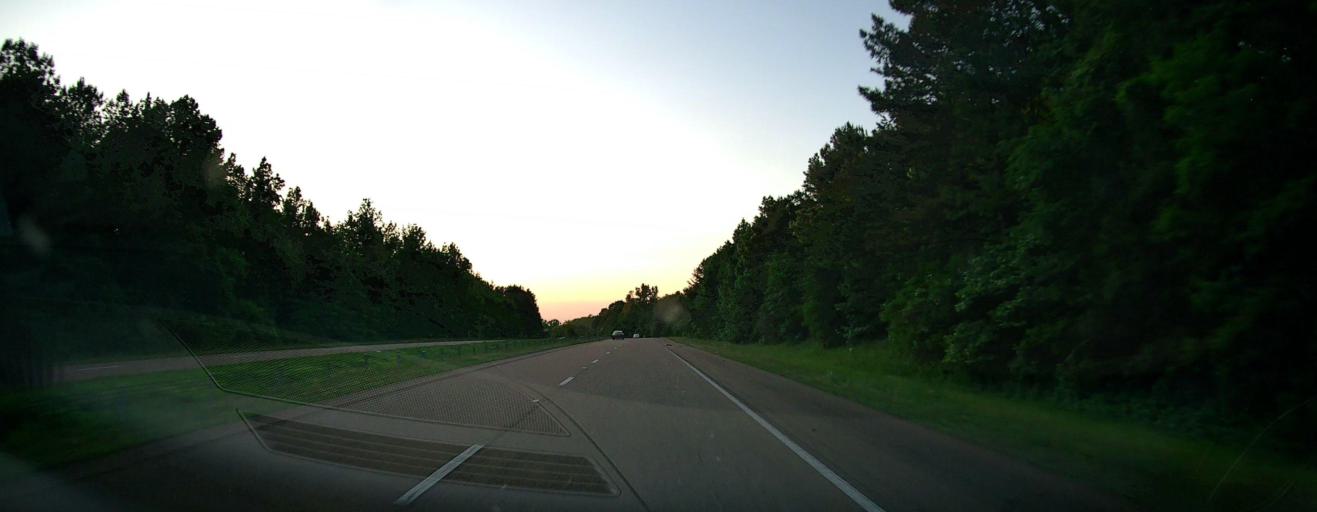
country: US
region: Mississippi
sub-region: Union County
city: New Albany
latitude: 34.4539
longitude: -88.9807
